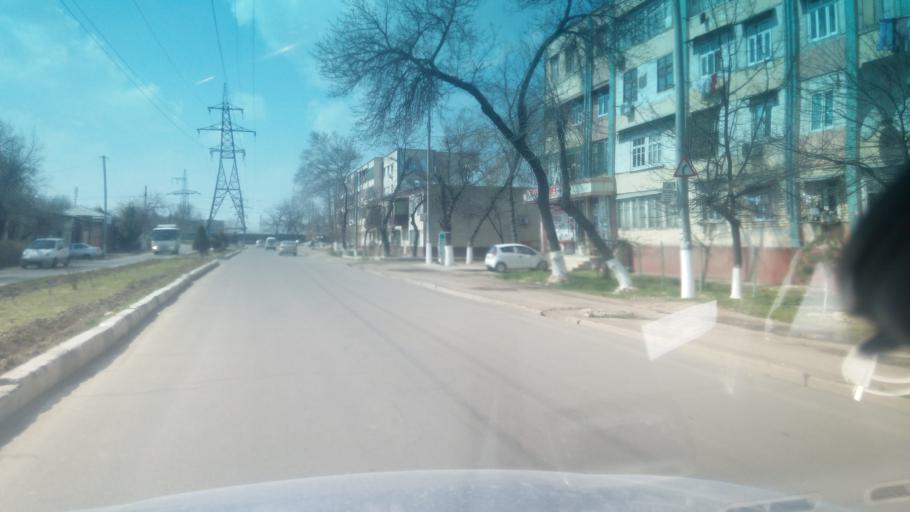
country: UZ
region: Toshkent Shahri
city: Bektemir
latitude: 41.2457
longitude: 69.3177
